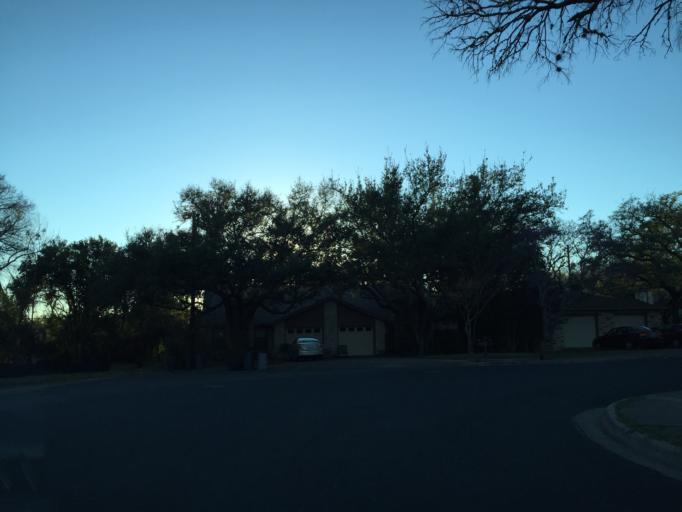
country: US
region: Texas
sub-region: Williamson County
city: Jollyville
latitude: 30.4348
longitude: -97.7786
